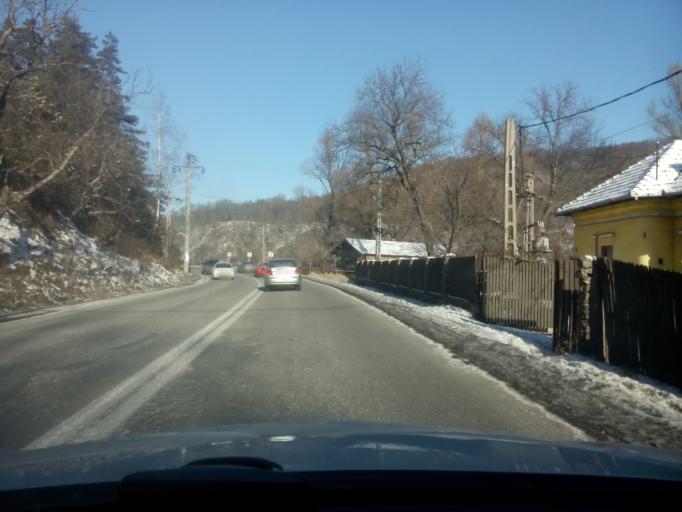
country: RO
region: Valcea
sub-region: Comuna Racovita
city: Racovita
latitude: 45.3751
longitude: 24.2955
